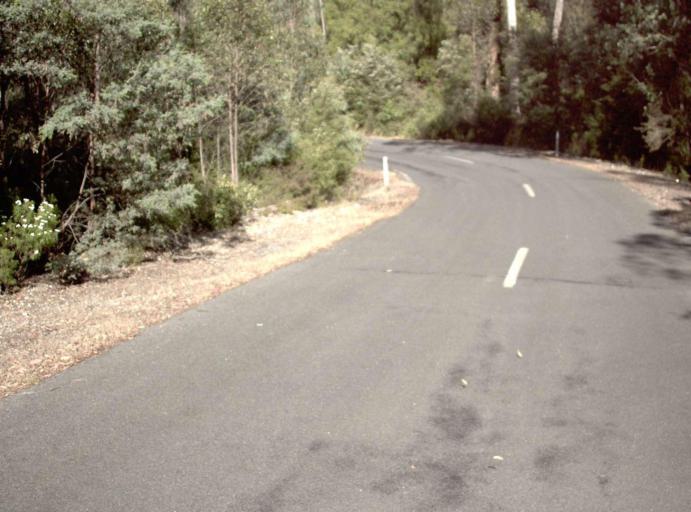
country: AU
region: Victoria
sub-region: East Gippsland
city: Lakes Entrance
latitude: -37.5023
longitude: 148.5475
